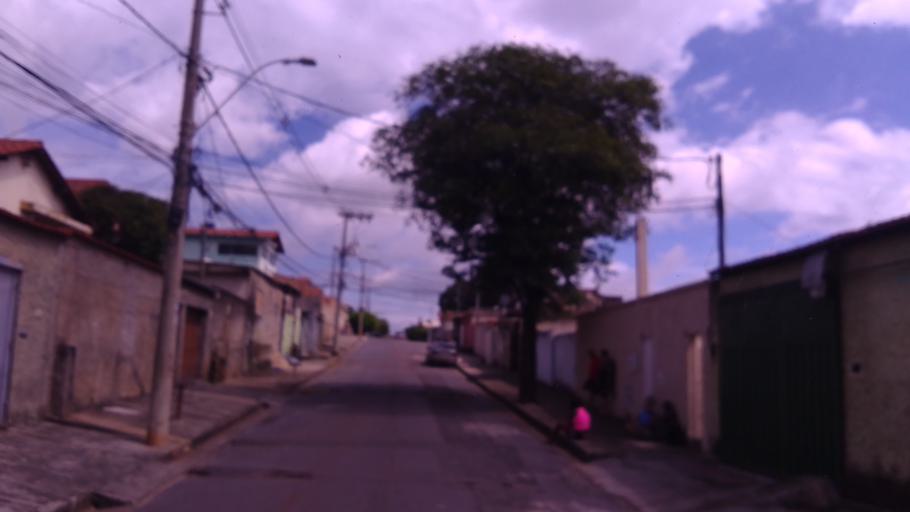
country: BR
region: Minas Gerais
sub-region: Contagem
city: Contagem
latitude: -19.9111
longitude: -44.0171
